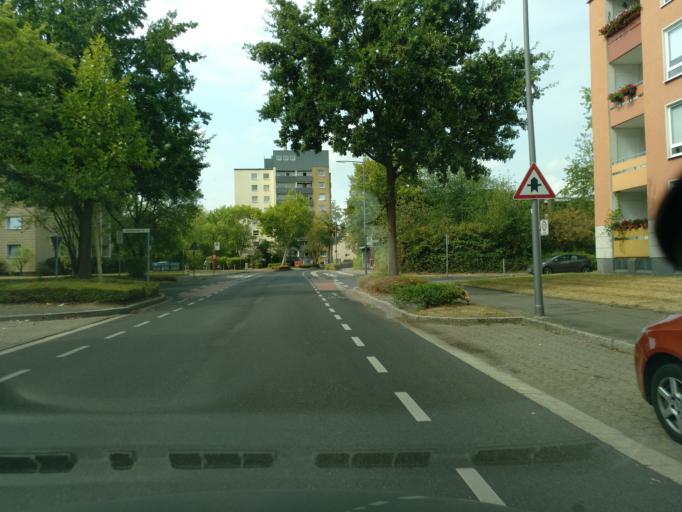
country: DE
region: North Rhine-Westphalia
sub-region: Regierungsbezirk Dusseldorf
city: Krefeld
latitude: 51.3048
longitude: 6.5781
